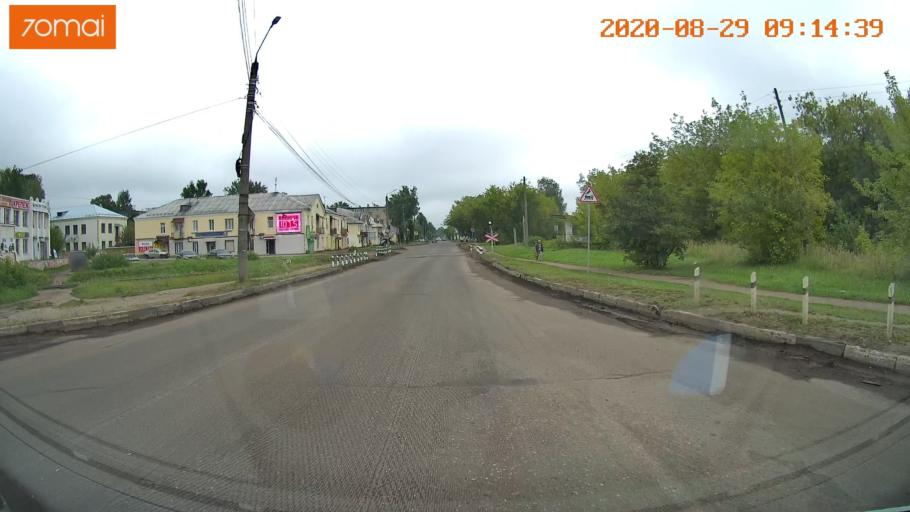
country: RU
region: Ivanovo
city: Kineshma
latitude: 57.4357
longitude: 42.1211
